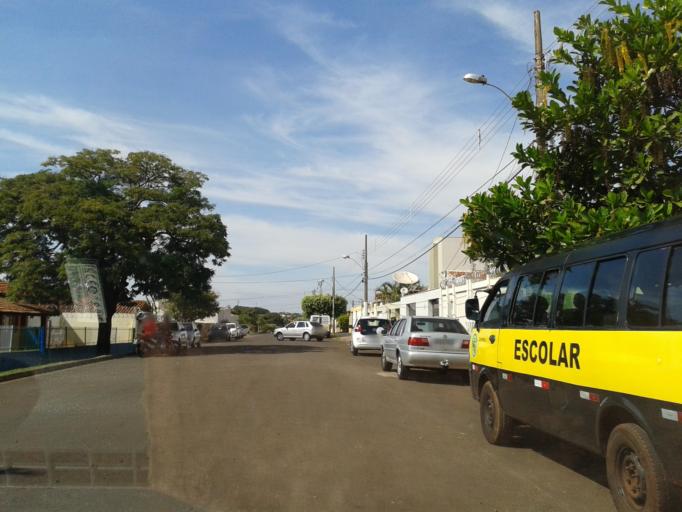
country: BR
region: Minas Gerais
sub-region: Ituiutaba
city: Ituiutaba
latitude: -18.9626
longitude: -49.4666
